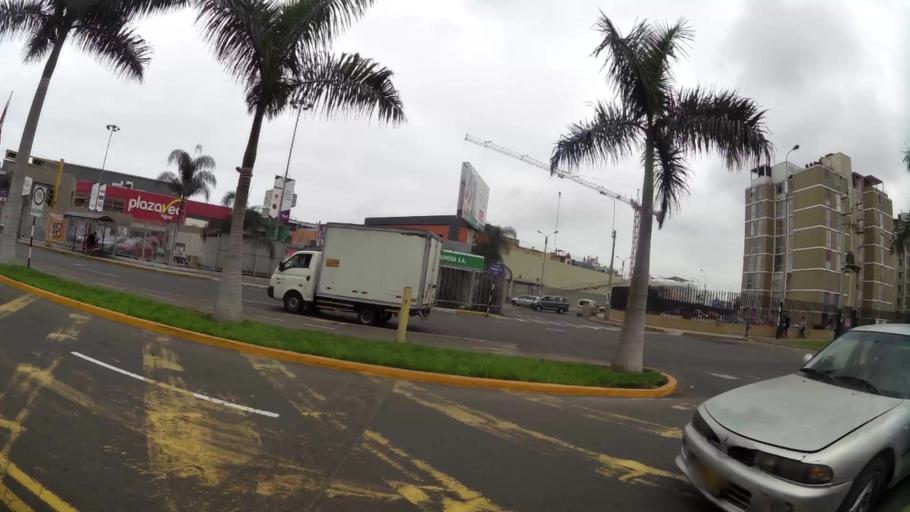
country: PE
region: Lima
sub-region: Lima
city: Surco
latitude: -12.1715
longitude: -76.9920
